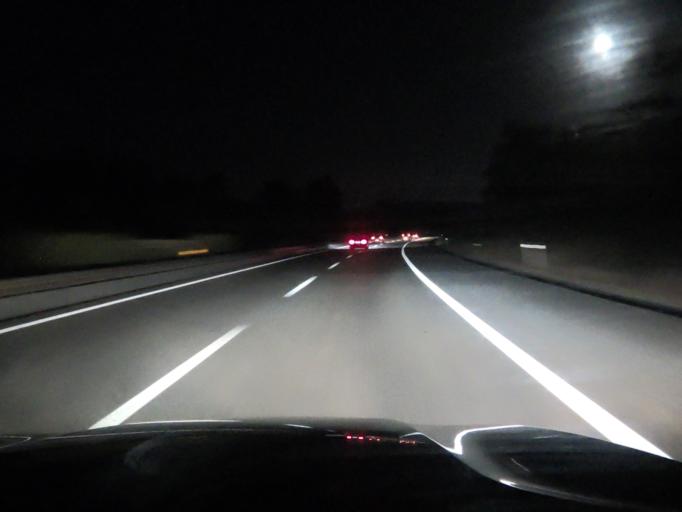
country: PT
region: Coimbra
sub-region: Condeixa-A-Nova
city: Condeixa-a-Nova
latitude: 40.0653
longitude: -8.5453
